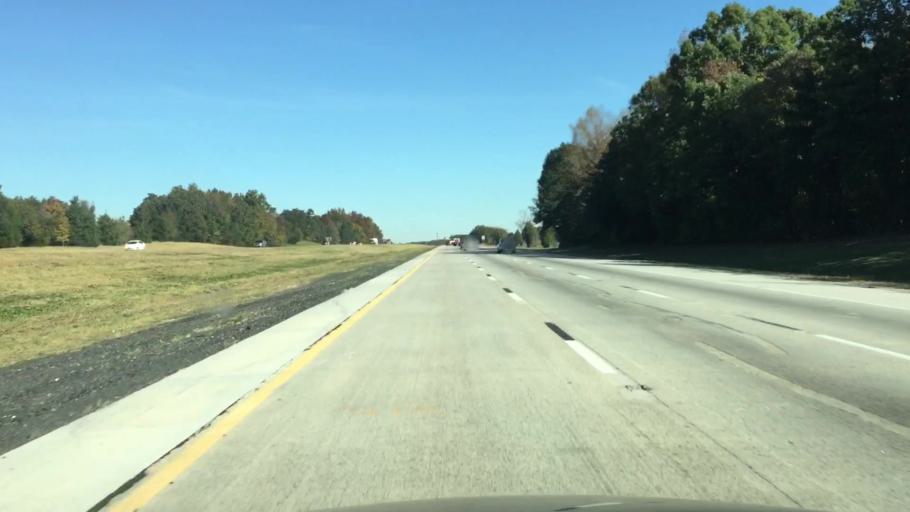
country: US
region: North Carolina
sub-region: Guilford County
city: Jamestown
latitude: 35.9543
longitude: -79.8974
